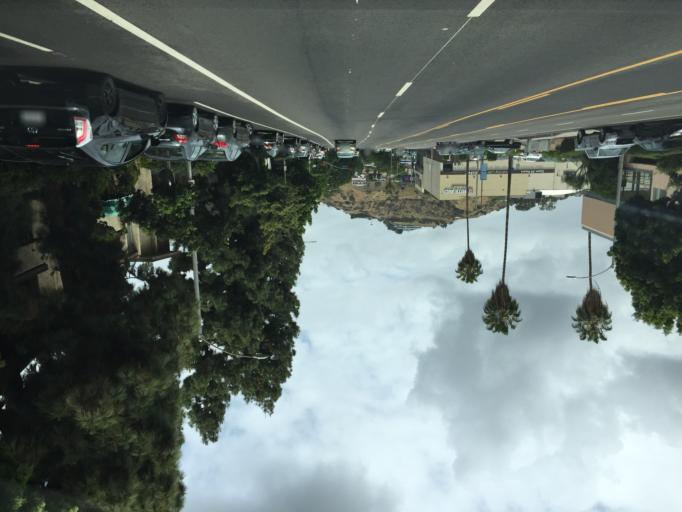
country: US
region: California
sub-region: Los Angeles County
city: West Hollywood
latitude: 34.0964
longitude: -118.3615
